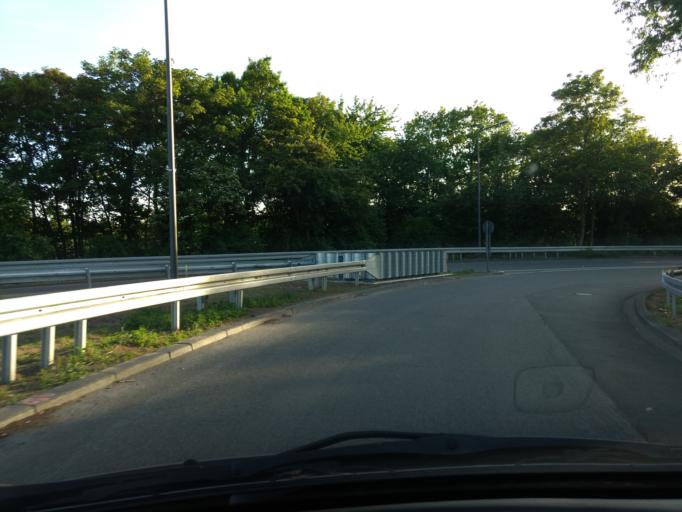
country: DE
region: North Rhine-Westphalia
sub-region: Regierungsbezirk Koln
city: Leverkusen
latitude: 51.0203
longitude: 6.9463
